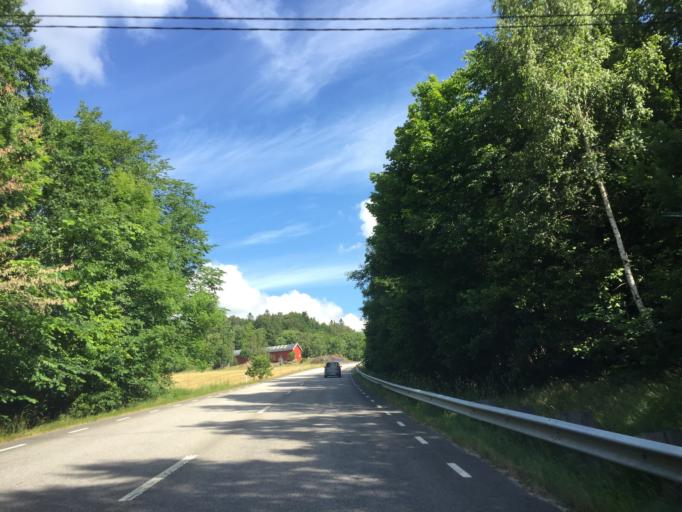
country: SE
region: Vaestra Goetaland
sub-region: Orust
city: Henan
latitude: 58.2782
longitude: 11.6939
